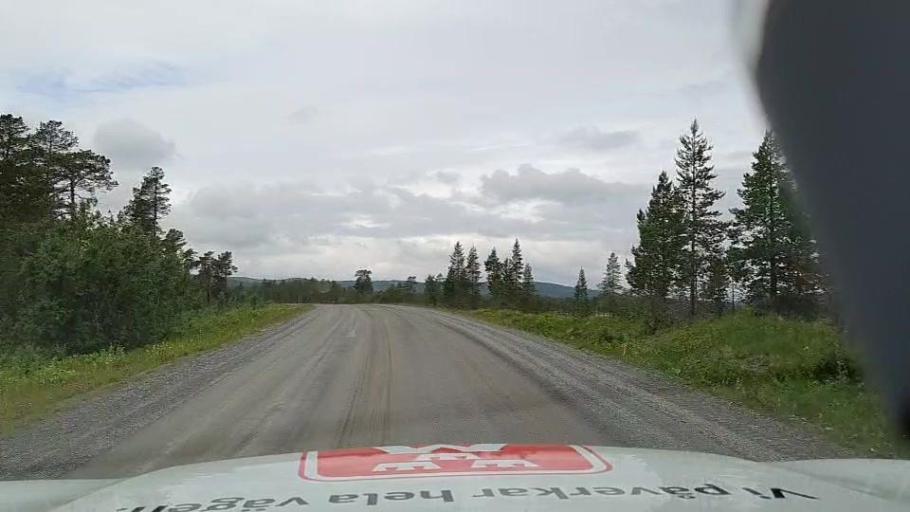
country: NO
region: Nord-Trondelag
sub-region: Snasa
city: Snaase
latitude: 63.7402
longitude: 12.4823
